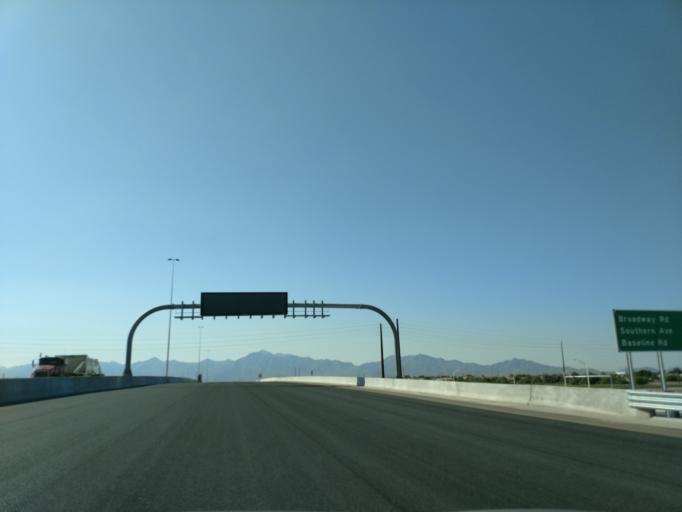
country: US
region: Arizona
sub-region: Maricopa County
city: Laveen
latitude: 33.4239
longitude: -112.1892
